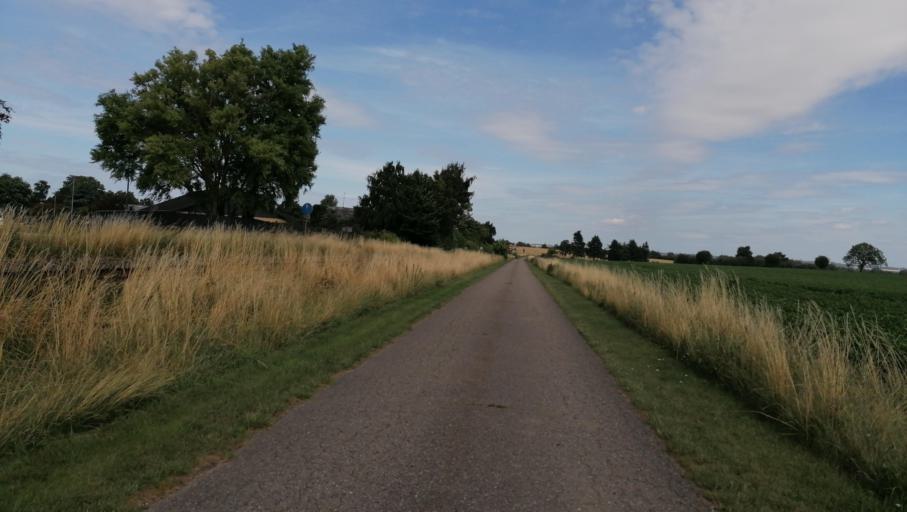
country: DK
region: Zealand
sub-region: Odsherred Kommune
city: Horve
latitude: 55.7560
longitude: 11.4578
